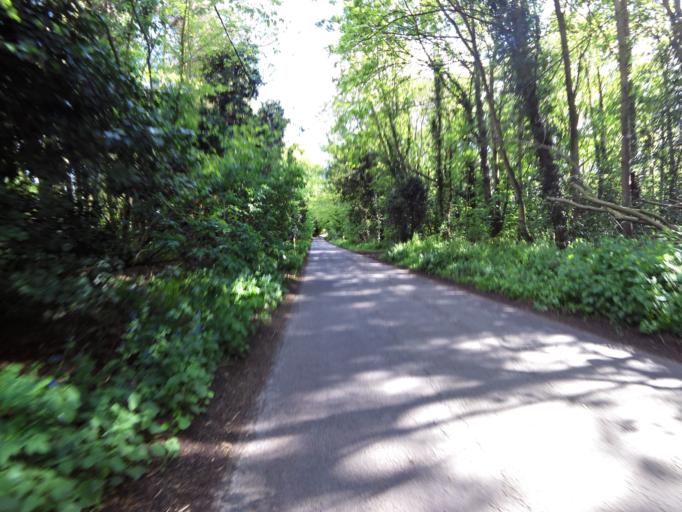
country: GB
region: England
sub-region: Suffolk
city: Thurston
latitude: 52.2448
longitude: 0.8262
